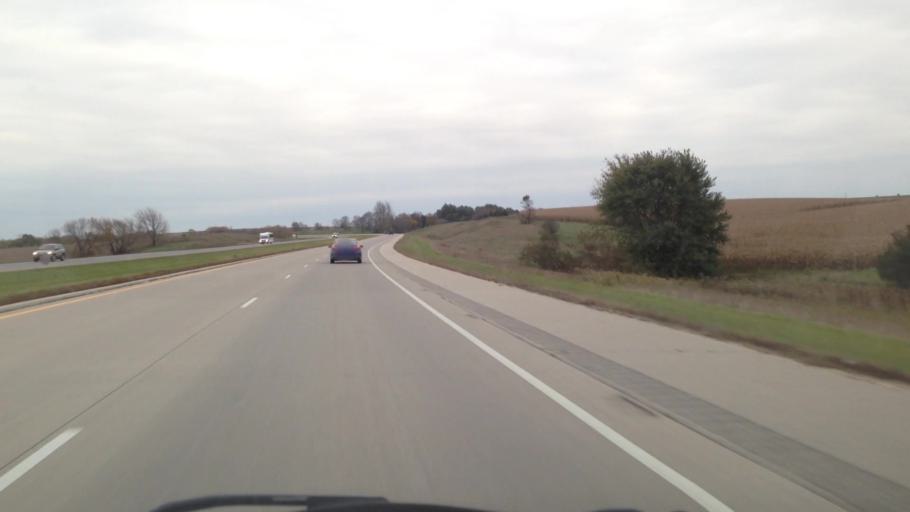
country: US
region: Minnesota
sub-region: Winona County
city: Saint Charles
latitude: 43.9389
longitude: -92.0189
